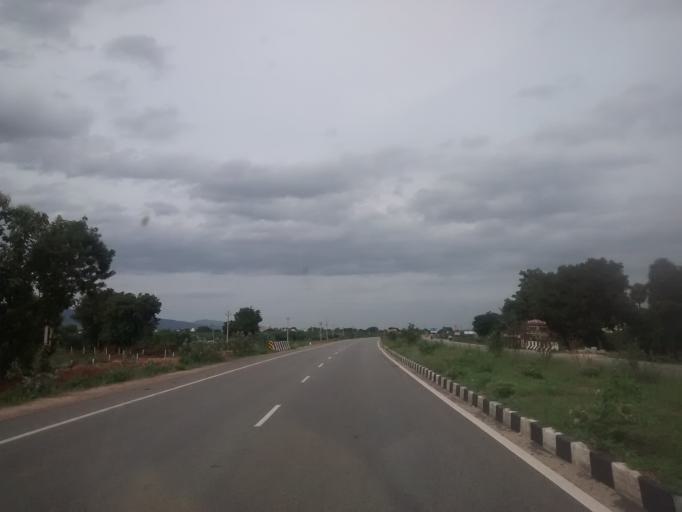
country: IN
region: Andhra Pradesh
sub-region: Chittoor
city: Narasingapuram
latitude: 13.6023
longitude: 79.3658
